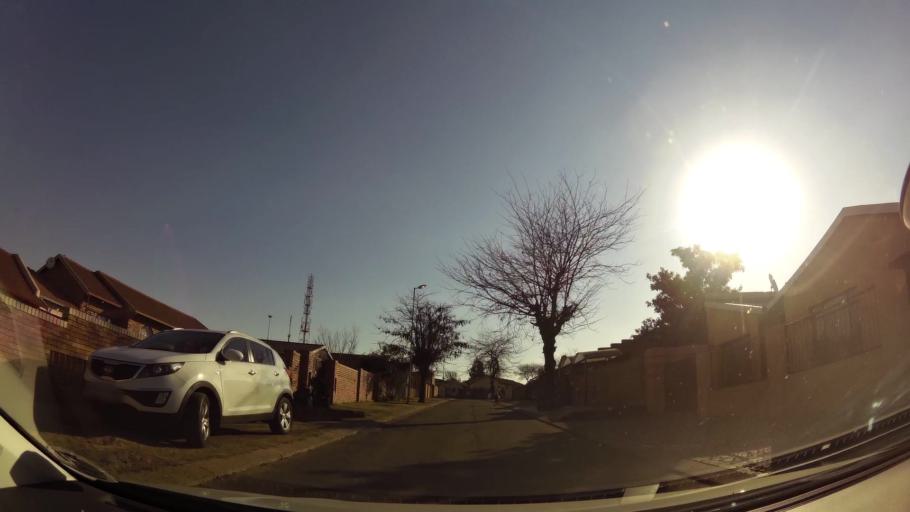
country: ZA
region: Gauteng
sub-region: City of Johannesburg Metropolitan Municipality
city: Soweto
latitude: -26.2698
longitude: 27.8776
